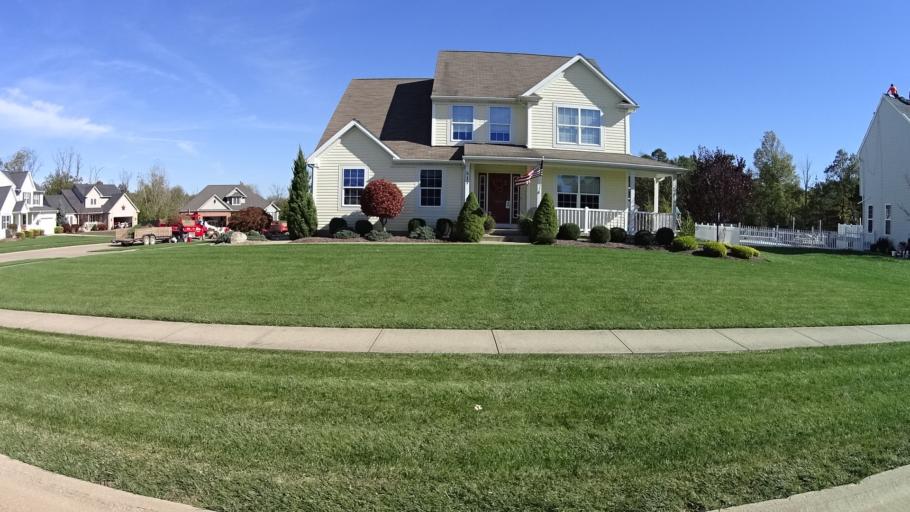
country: US
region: Ohio
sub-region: Lorain County
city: Amherst
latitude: 41.3845
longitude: -82.2413
